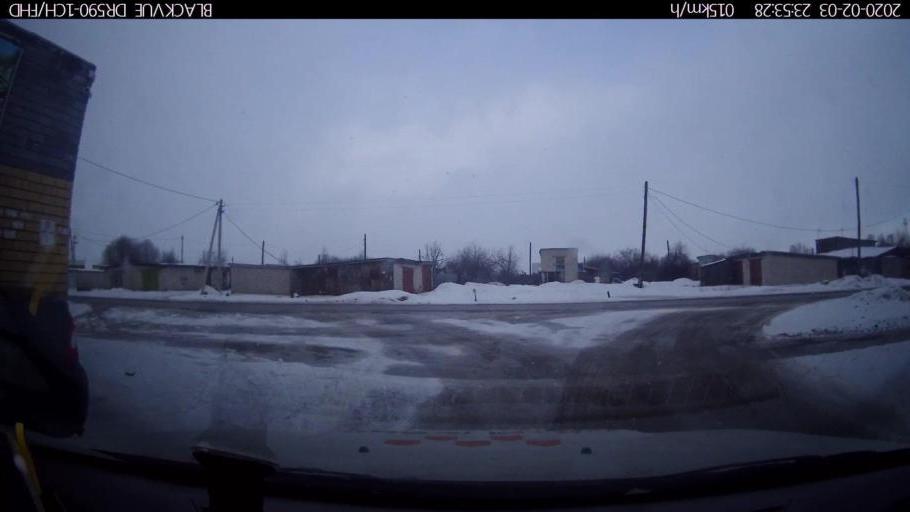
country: RU
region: Nizjnij Novgorod
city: Dal'neye Konstantinovo
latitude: 55.8065
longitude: 44.0784
